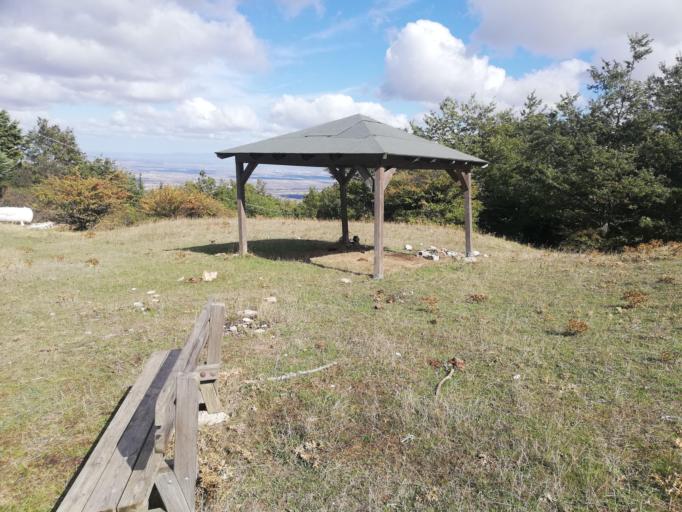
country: IT
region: Apulia
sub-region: Provincia di Foggia
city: Castelluccio Valmaggiore
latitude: 41.3686
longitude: 15.1722
